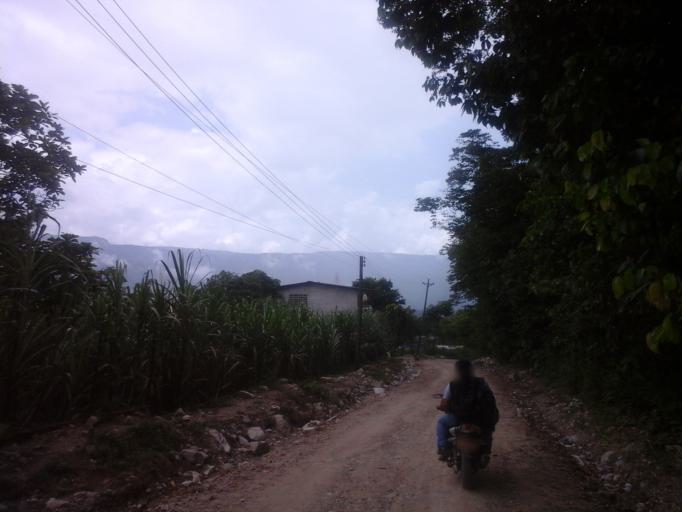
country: CO
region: Putumayo
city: Mocoa
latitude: 1.1790
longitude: -76.6667
